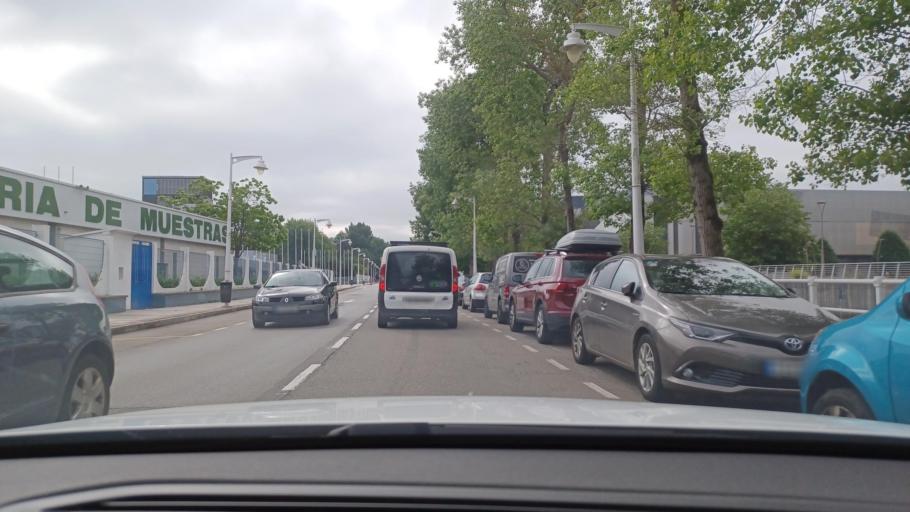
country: ES
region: Asturias
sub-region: Province of Asturias
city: Gijon
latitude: 43.5381
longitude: -5.6393
